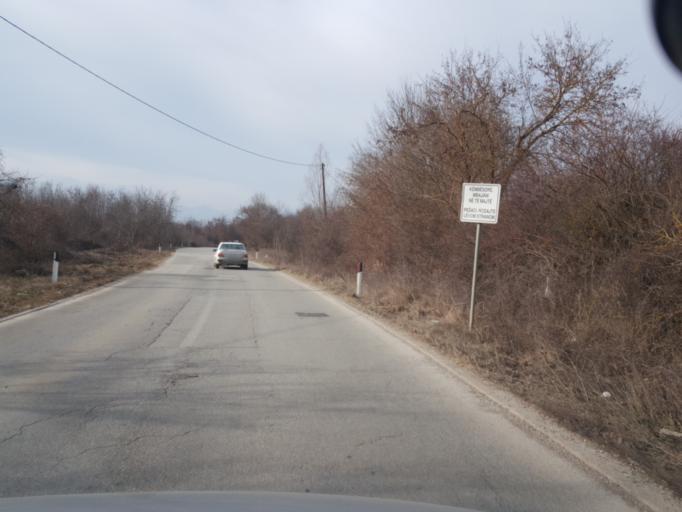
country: XK
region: Pec
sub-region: Komuna e Klines
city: Klina
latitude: 42.6722
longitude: 20.5325
